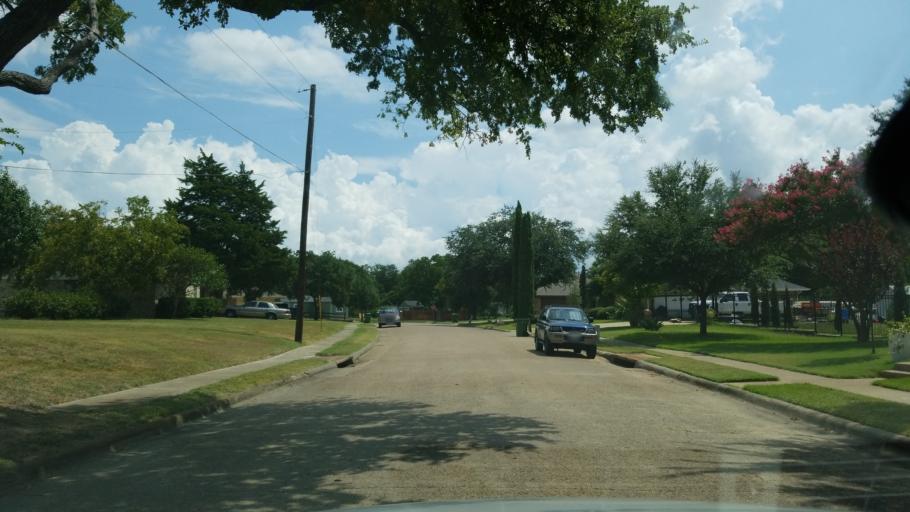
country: US
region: Texas
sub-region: Dallas County
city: Garland
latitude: 32.9203
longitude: -96.6585
